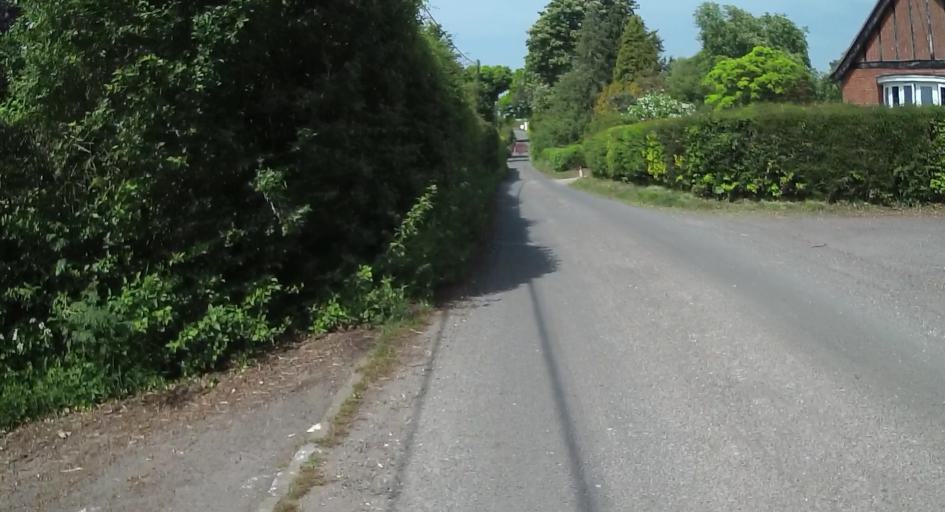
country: GB
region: England
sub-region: Hampshire
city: Overton
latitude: 51.2605
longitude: -1.2318
